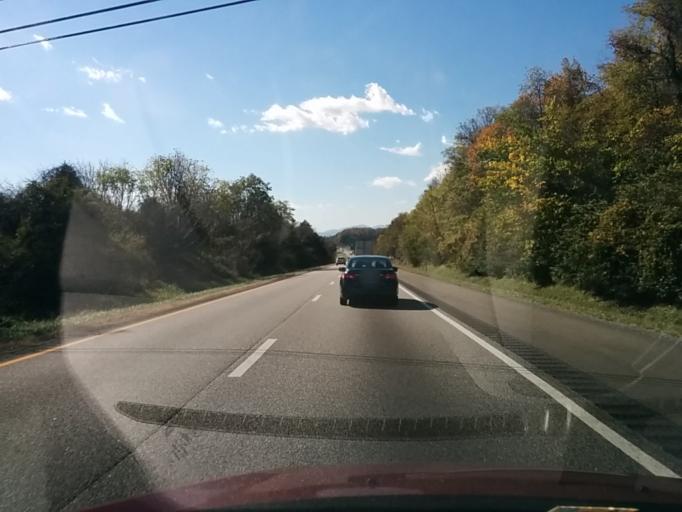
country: US
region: Virginia
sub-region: Botetourt County
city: Daleville
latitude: 37.3975
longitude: -79.9001
